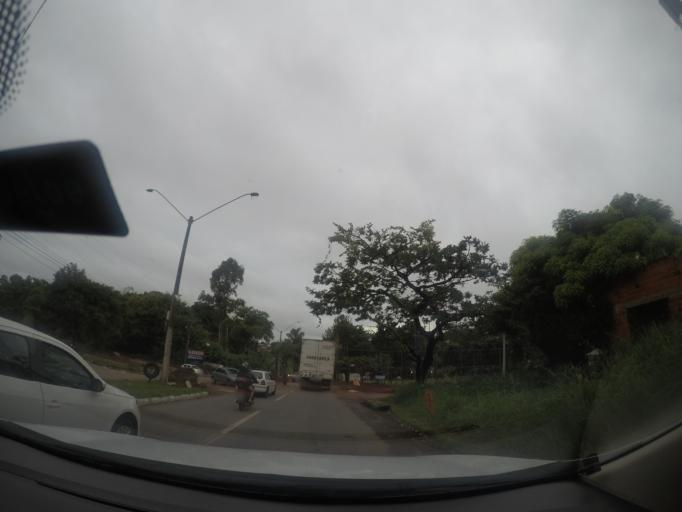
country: BR
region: Goias
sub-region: Aparecida De Goiania
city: Aparecida de Goiania
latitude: -16.7584
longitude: -49.3224
